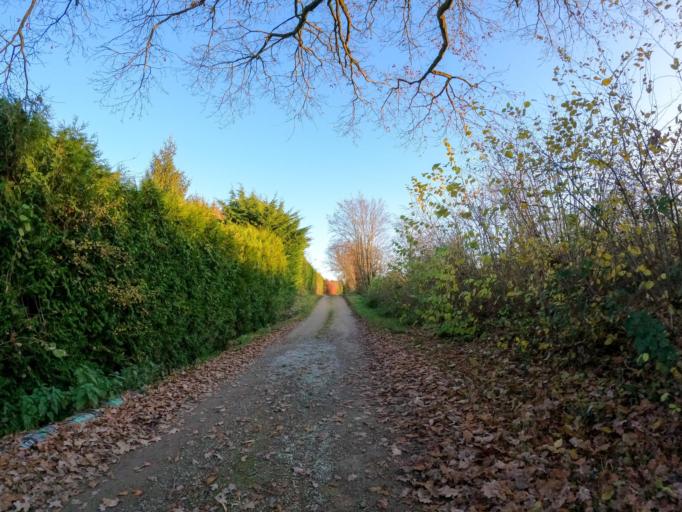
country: LU
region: Luxembourg
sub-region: Canton de Capellen
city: Dippach
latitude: 49.5935
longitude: 5.9909
